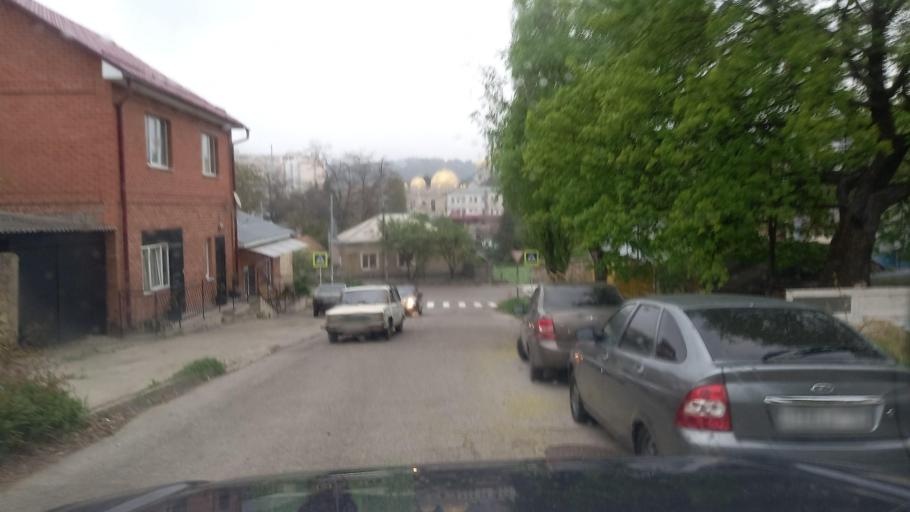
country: RU
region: Stavropol'skiy
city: Kislovodsk
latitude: 43.8952
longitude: 42.7106
